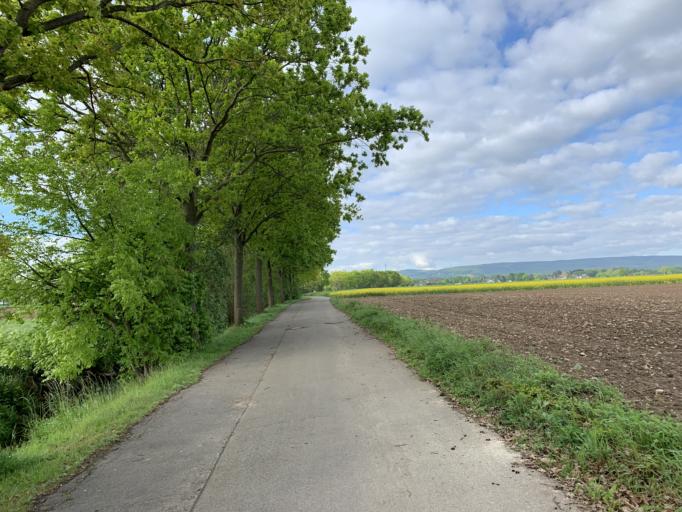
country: DE
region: North Rhine-Westphalia
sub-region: Regierungsbezirk Koln
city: Dueren
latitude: 50.7828
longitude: 6.4612
